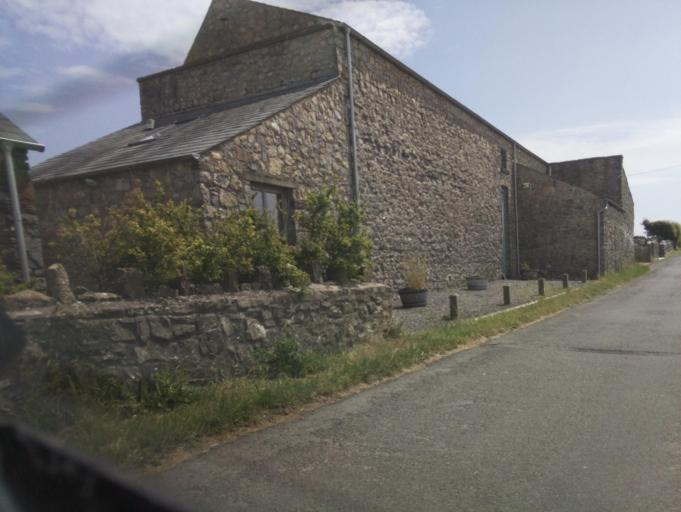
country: GB
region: Wales
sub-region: Vale of Glamorgan
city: Wick
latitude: 51.4394
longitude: -3.5683
